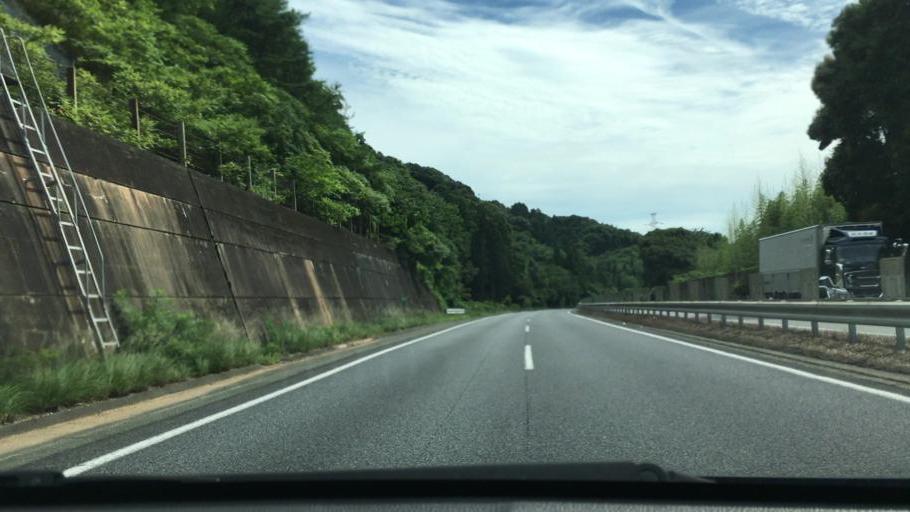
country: JP
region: Yamaguchi
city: Ogori-shimogo
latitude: 34.1262
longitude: 131.4204
